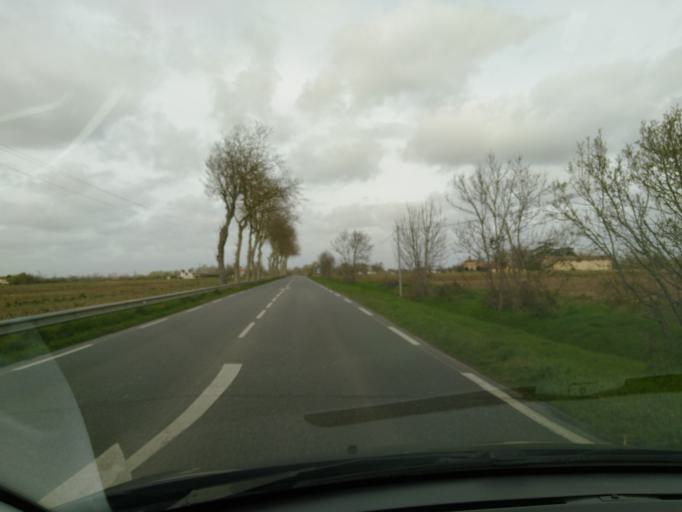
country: FR
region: Midi-Pyrenees
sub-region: Departement de la Haute-Garonne
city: Merville
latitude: 43.7406
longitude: 1.3114
